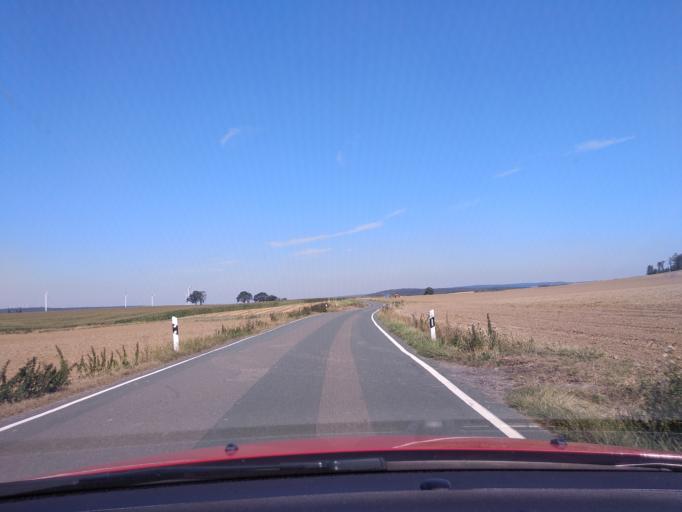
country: DE
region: North Rhine-Westphalia
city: Beverungen
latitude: 51.6726
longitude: 9.2978
